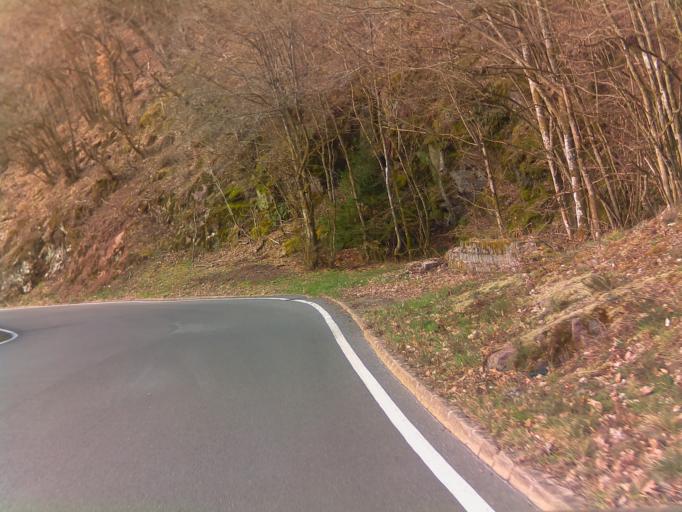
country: DE
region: Rheinland-Pfalz
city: Frauenberg
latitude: 49.6702
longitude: 7.2716
